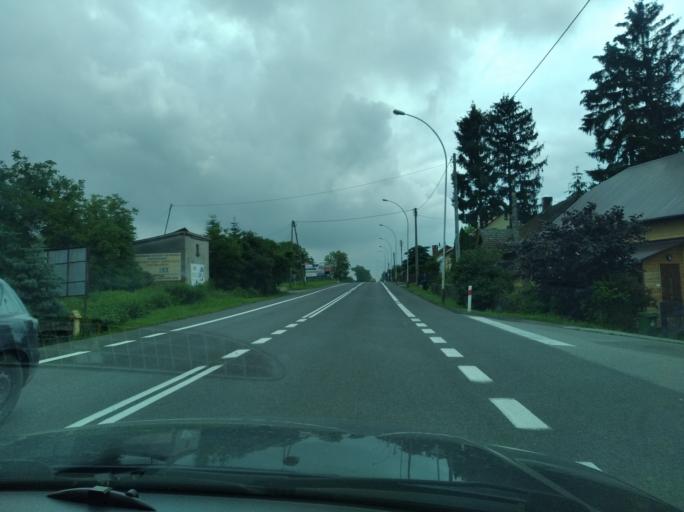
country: PL
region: Subcarpathian Voivodeship
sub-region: Powiat przeworski
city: Przeworsk
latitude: 50.0558
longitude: 22.5076
